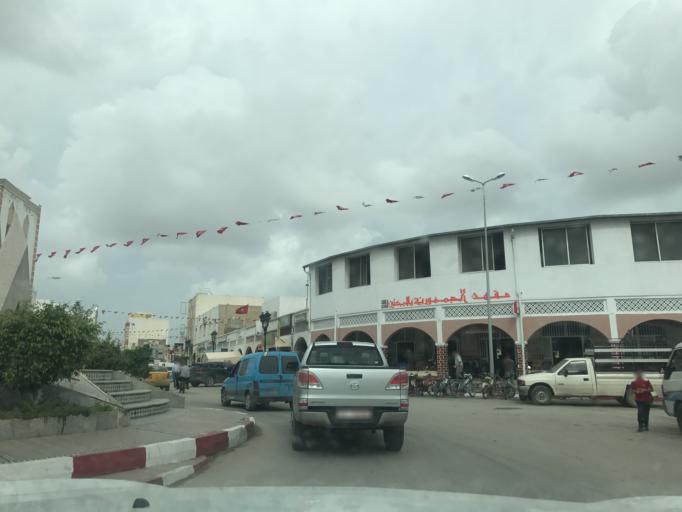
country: TN
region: Al Munastir
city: Qasr Hallal
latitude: 35.6278
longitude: 10.9004
